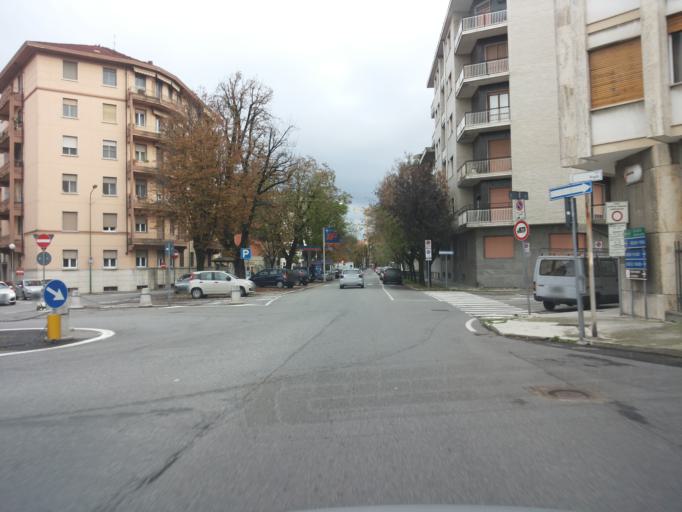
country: IT
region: Piedmont
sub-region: Provincia di Alessandria
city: Casale Monferrato
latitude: 45.1339
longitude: 8.4473
